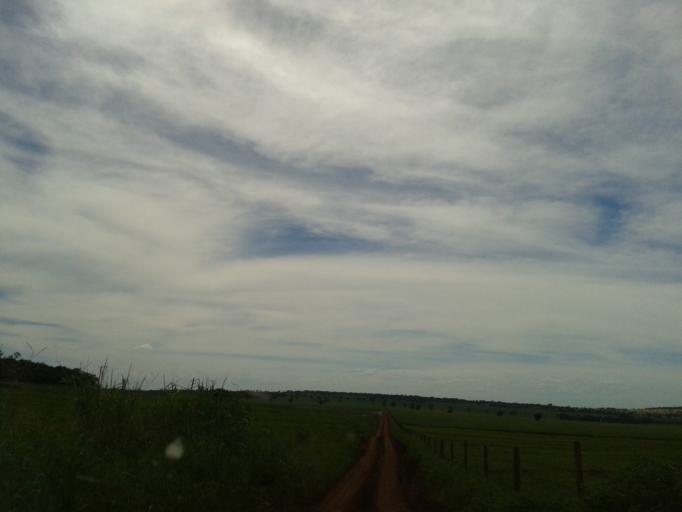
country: BR
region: Minas Gerais
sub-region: Capinopolis
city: Capinopolis
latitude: -18.7480
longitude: -49.8355
